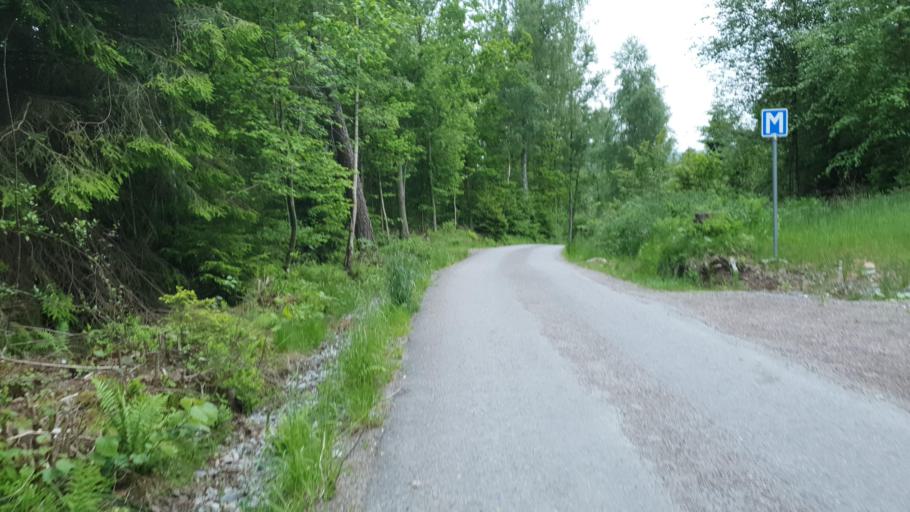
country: SE
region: Vaestra Goetaland
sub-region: Molndal
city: Kallered
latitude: 57.6147
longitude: 12.0583
